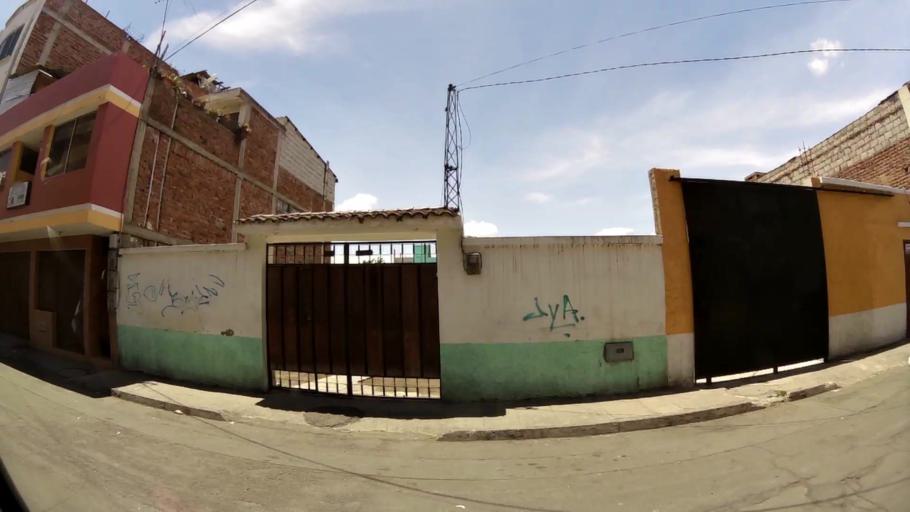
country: EC
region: Chimborazo
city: Riobamba
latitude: -1.6751
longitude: -78.6564
